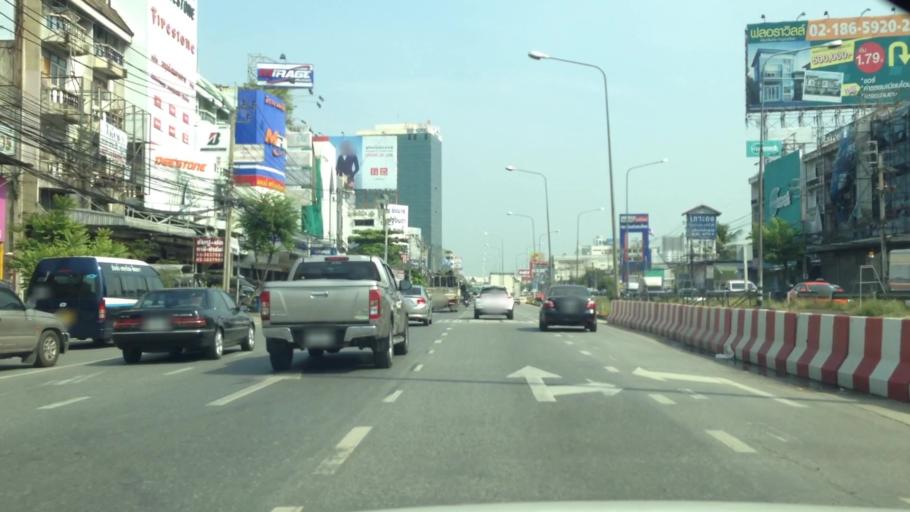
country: TH
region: Bangkok
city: Bang Na
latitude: 13.6446
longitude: 100.6368
